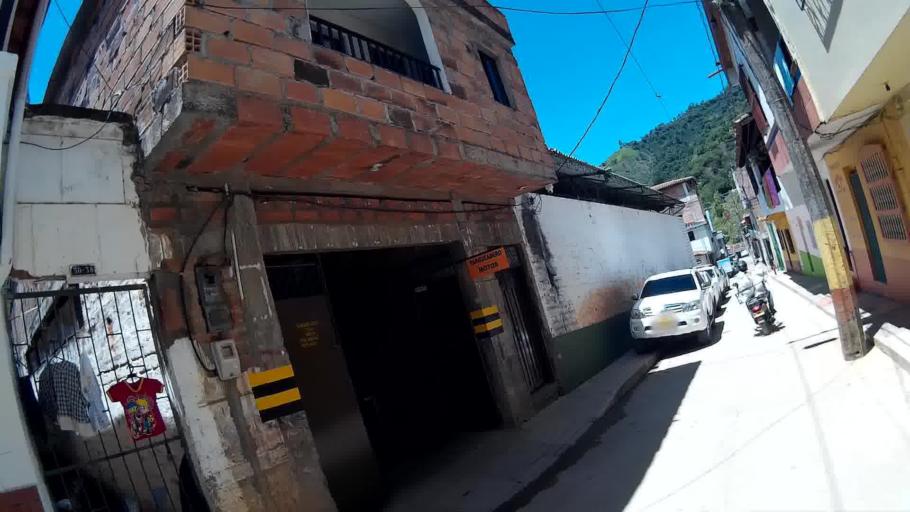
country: CO
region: Antioquia
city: Salgar
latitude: 5.9624
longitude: -75.9796
